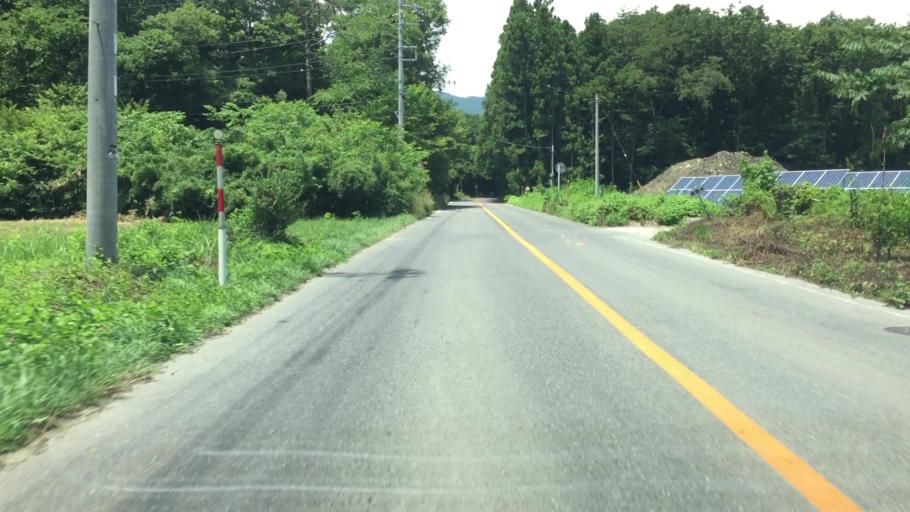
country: JP
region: Tochigi
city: Kuroiso
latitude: 37.0192
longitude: 139.9522
